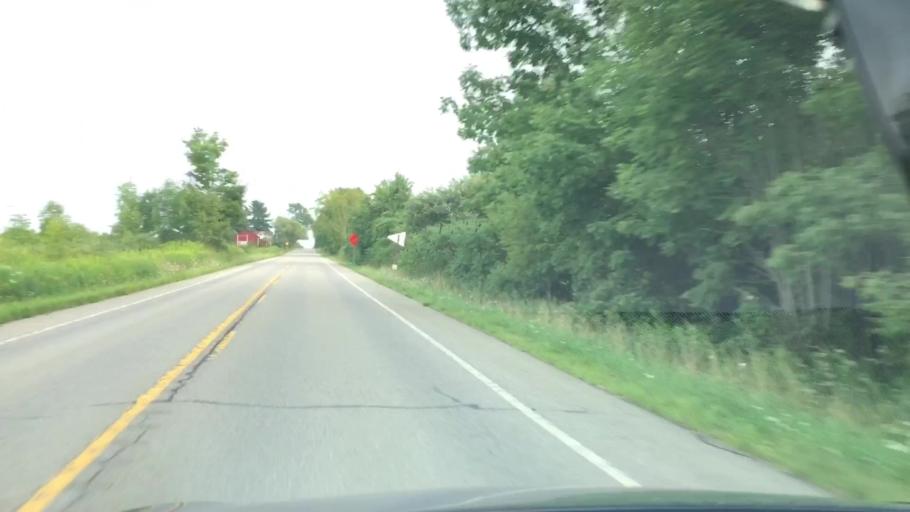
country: US
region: Pennsylvania
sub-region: Erie County
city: Union City
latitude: 41.8132
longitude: -79.8025
